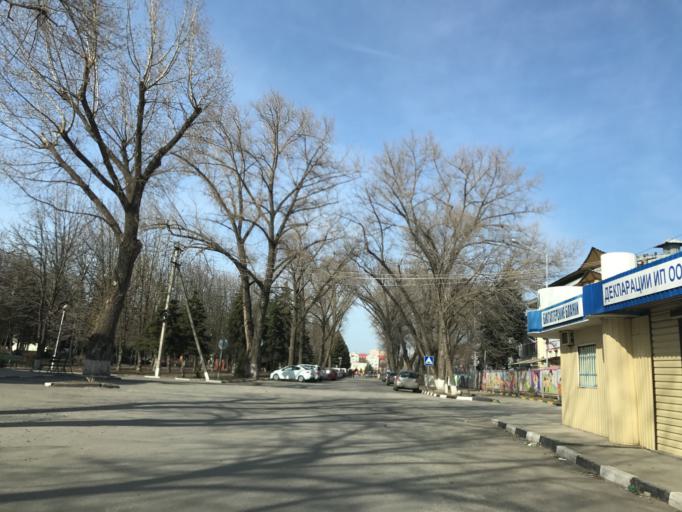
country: RU
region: Rostov
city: Bataysk
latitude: 47.1357
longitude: 39.7453
